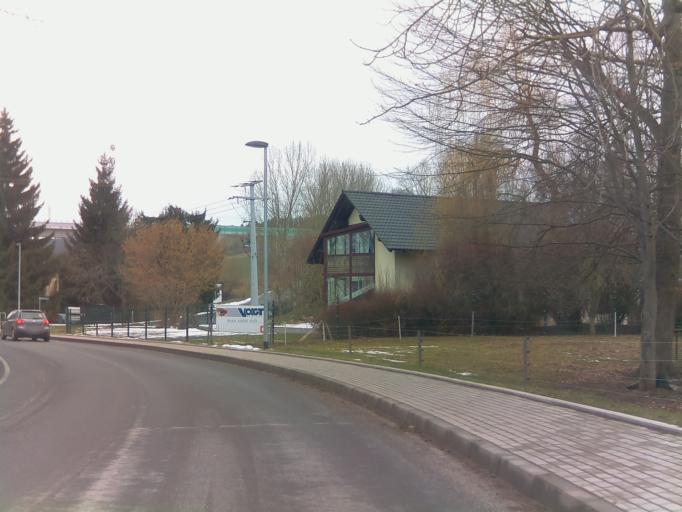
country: DE
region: Thuringia
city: Langewiesen
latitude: 50.7000
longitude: 11.0126
